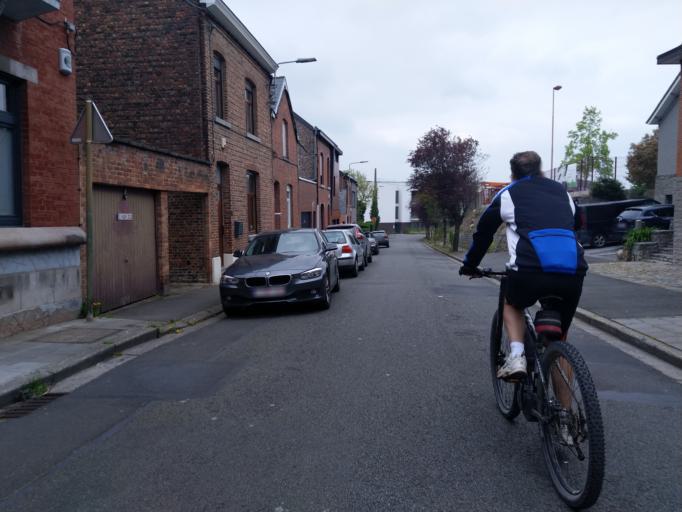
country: BE
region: Wallonia
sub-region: Province du Hainaut
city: Mons
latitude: 50.4422
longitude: 3.9443
